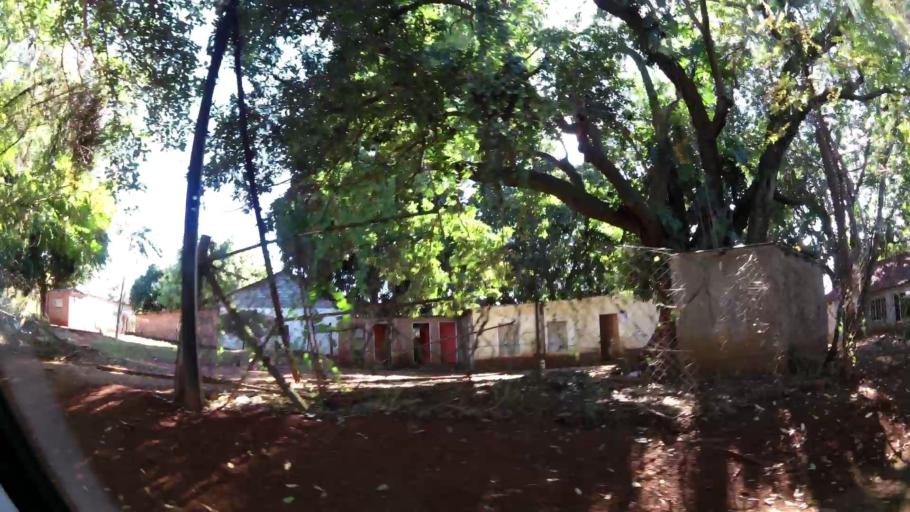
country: ZA
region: Limpopo
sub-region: Mopani District Municipality
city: Tzaneen
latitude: -23.8204
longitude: 30.1562
